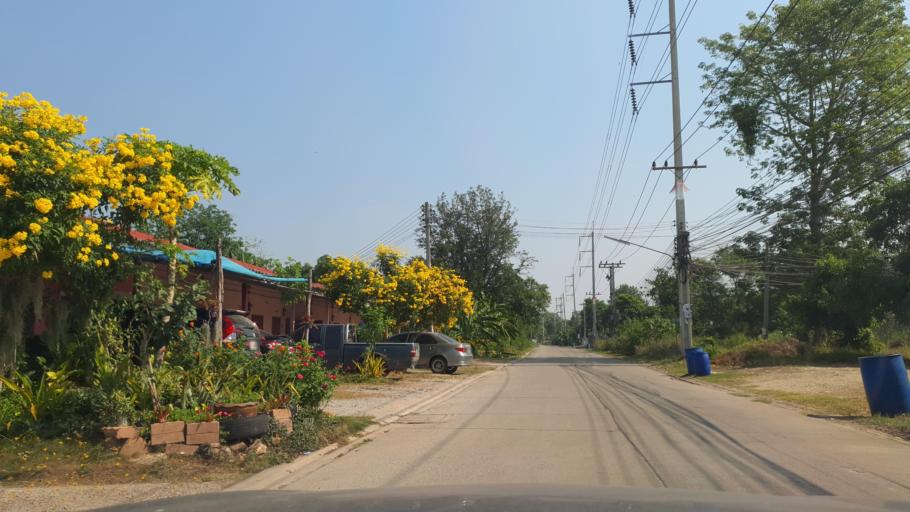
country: TH
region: Kanchanaburi
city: Kanchanaburi
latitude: 14.0646
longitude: 99.4857
